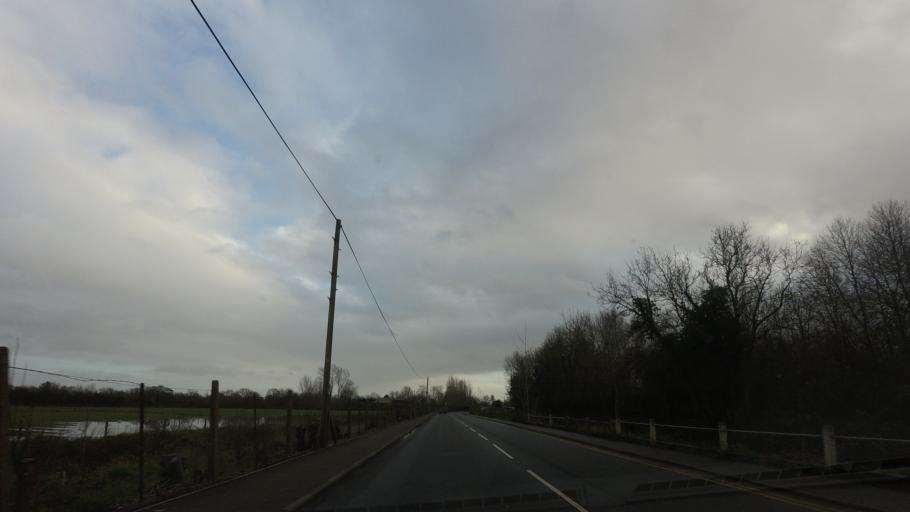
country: GB
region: England
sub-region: Kent
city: Yalding
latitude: 51.2251
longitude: 0.4177
